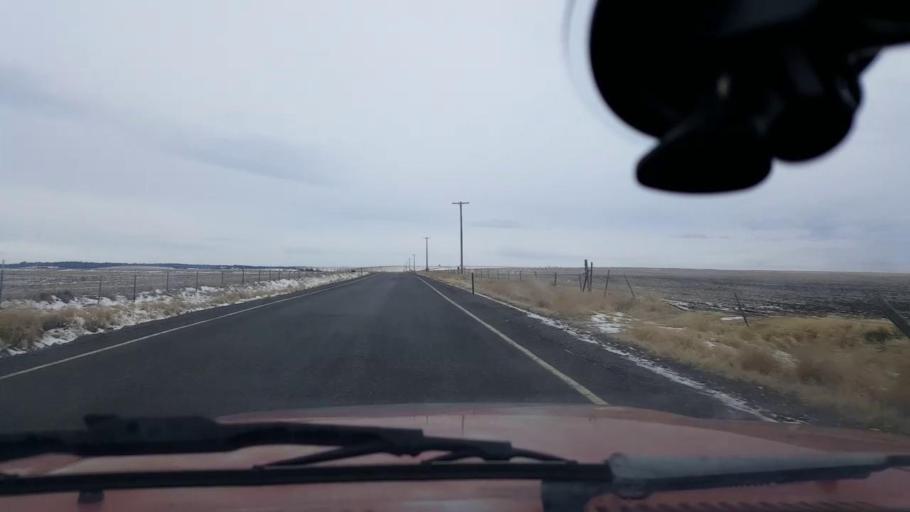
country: US
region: Washington
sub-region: Garfield County
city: Pomeroy
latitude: 46.3220
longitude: -117.3776
